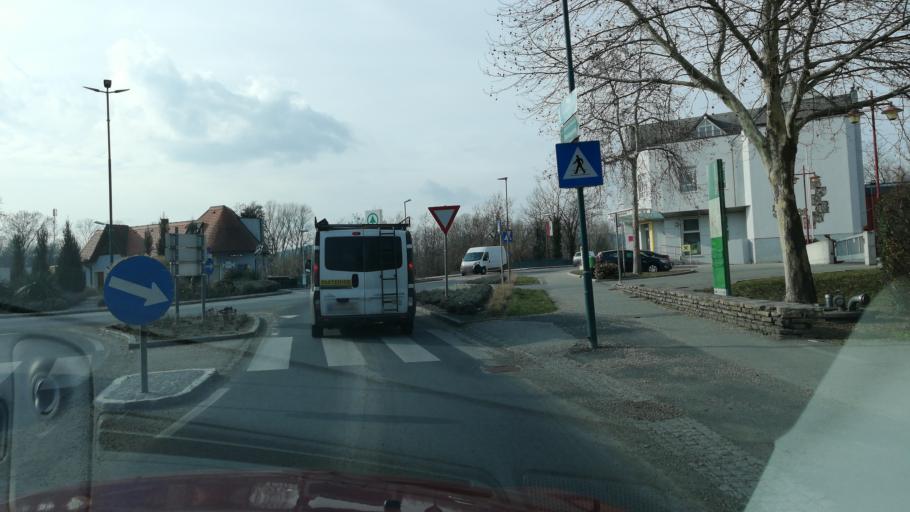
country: AT
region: Lower Austria
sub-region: Politischer Bezirk Sankt Polten
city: Traismauer
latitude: 48.3513
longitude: 15.7435
